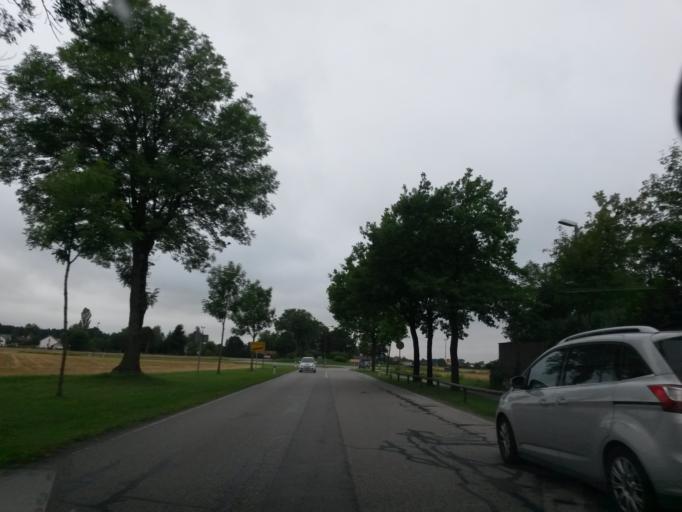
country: DE
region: Bavaria
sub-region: Upper Bavaria
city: Putzbrunn
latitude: 48.0778
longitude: 11.7100
